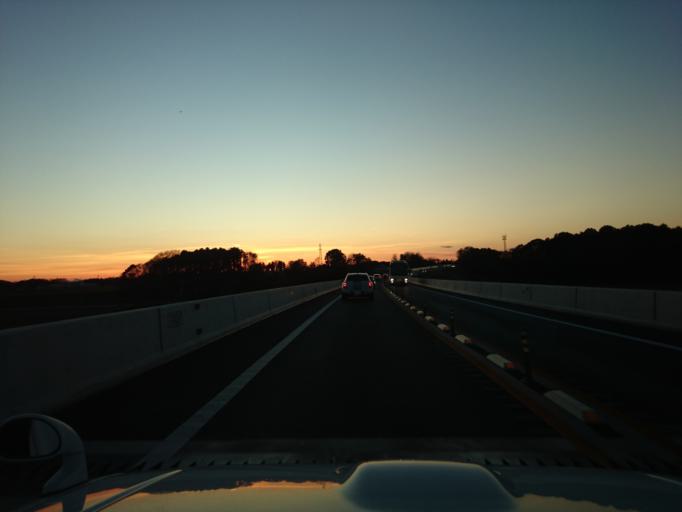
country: JP
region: Ibaraki
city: Ishige
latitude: 36.0739
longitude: 139.9696
